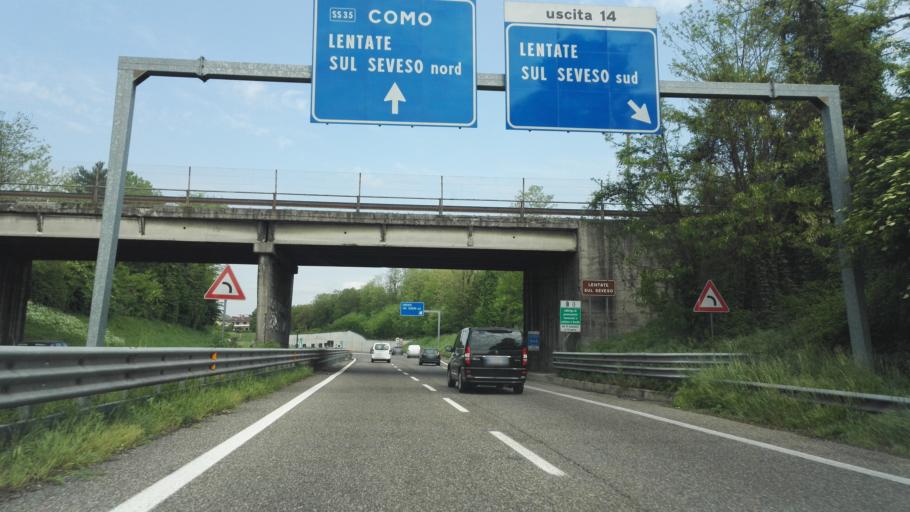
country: IT
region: Lombardy
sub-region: Provincia di Monza e Brianza
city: Barlassina
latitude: 45.6631
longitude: 9.1293
